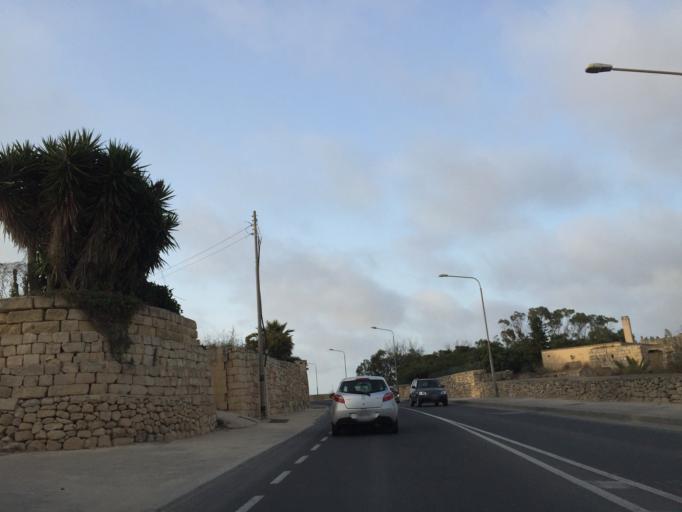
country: MT
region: Il-Mosta
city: Mosta
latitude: 35.9117
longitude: 14.4139
